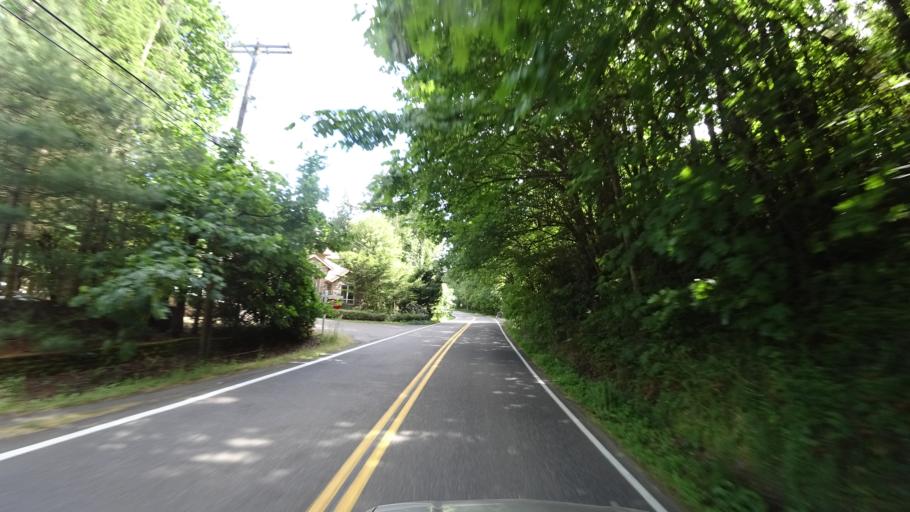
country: US
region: Oregon
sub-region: Washington County
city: Bethany
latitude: 45.6031
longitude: -122.8327
